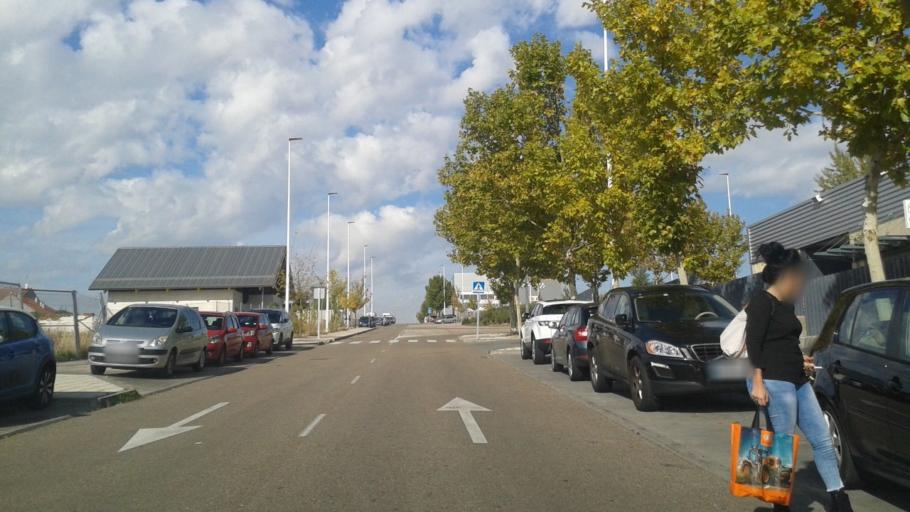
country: ES
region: Castille and Leon
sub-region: Provincia de Valladolid
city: Arroyo
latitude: 41.6259
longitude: -4.7654
